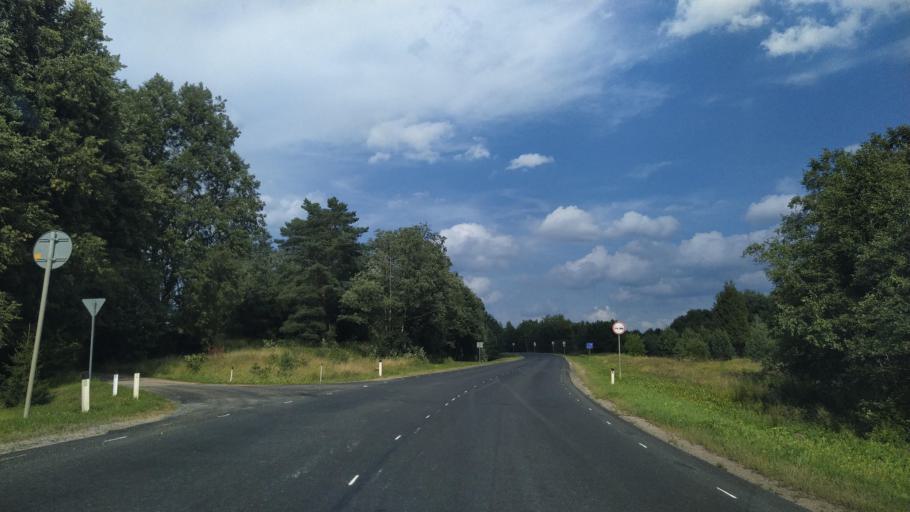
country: RU
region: Pskov
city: Porkhov
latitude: 57.8130
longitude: 29.5042
